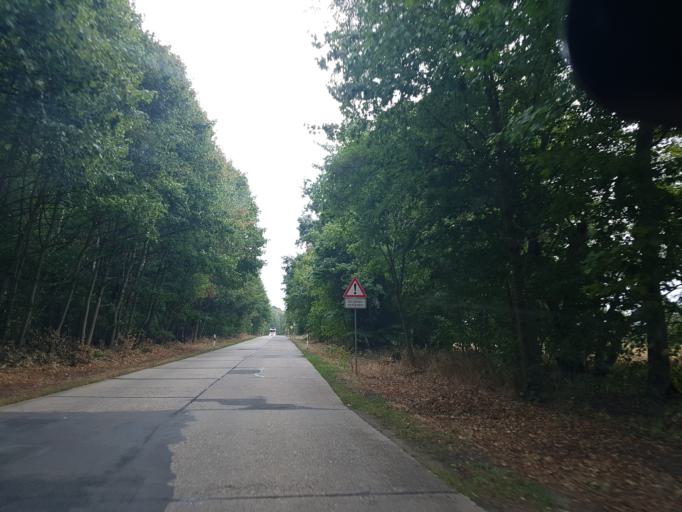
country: DE
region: Saxony-Anhalt
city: Lindau
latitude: 52.0748
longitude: 12.2438
